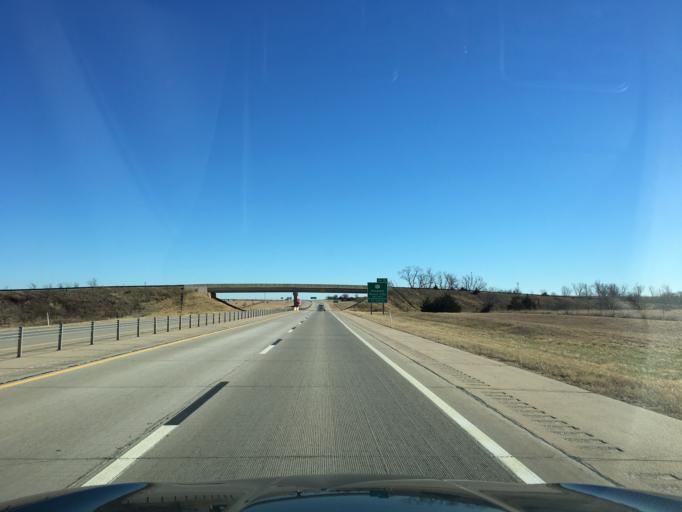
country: US
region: Oklahoma
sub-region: Noble County
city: Perry
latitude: 36.3870
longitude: -97.0879
